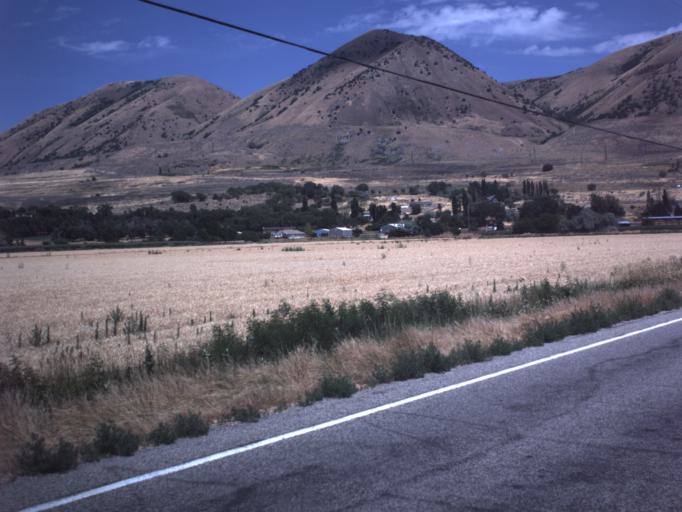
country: US
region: Utah
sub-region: Box Elder County
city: Elwood
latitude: 41.7153
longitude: -112.1019
